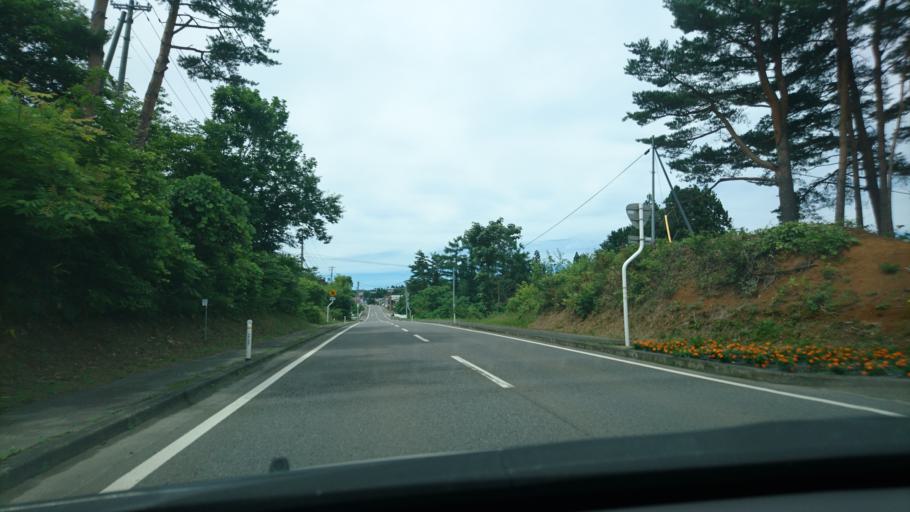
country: JP
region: Iwate
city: Miyako
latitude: 39.9210
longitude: 141.9025
